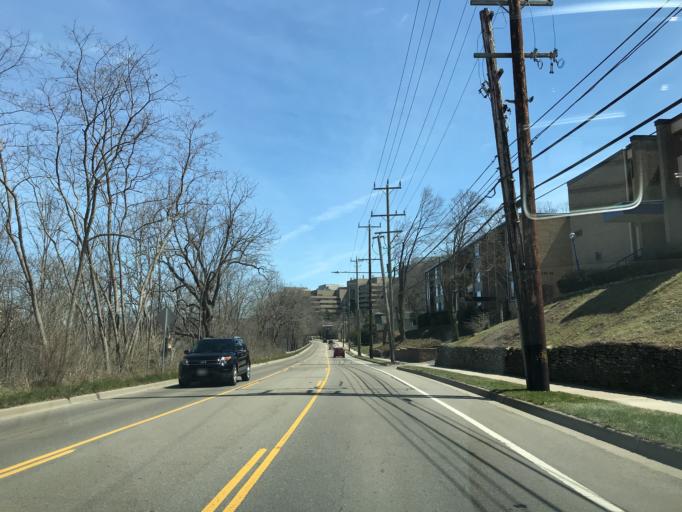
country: US
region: Michigan
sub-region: Washtenaw County
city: Ann Arbor
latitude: 42.2864
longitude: -83.7400
